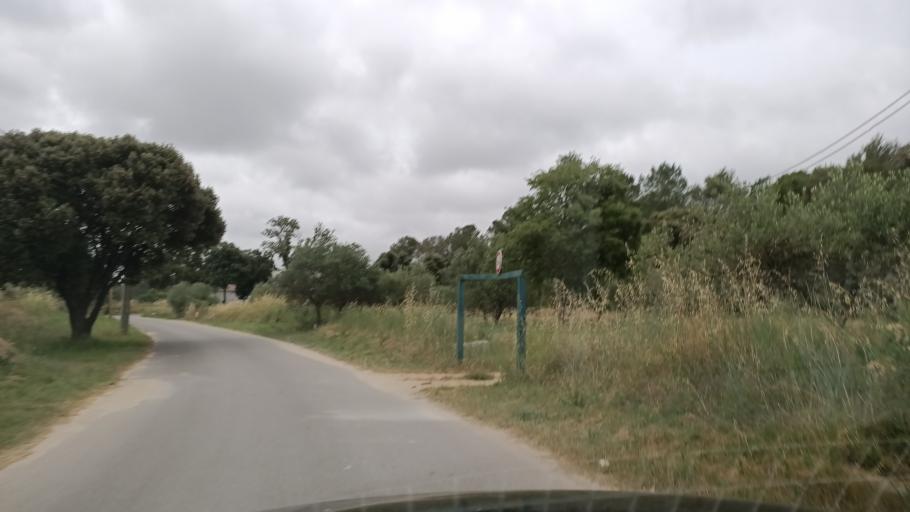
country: FR
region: Languedoc-Roussillon
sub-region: Departement de l'Herault
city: Castries
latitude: 43.6928
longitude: 3.9962
